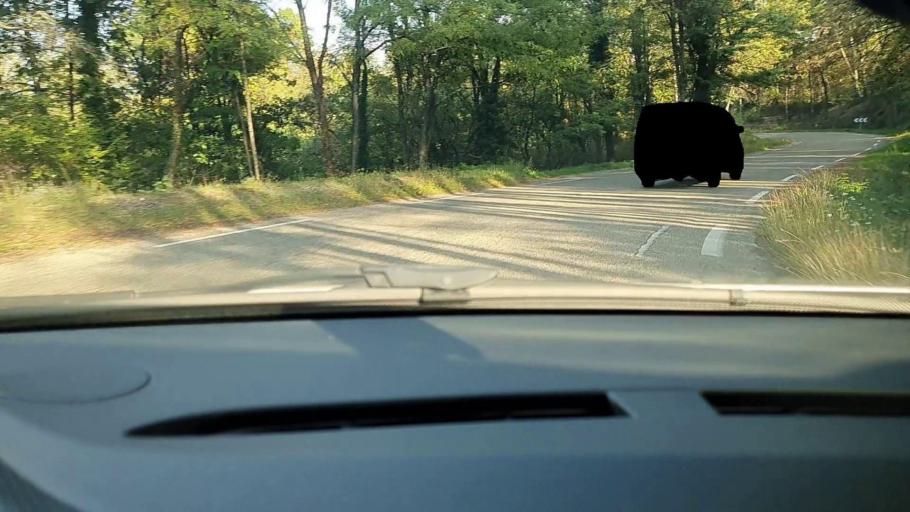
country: FR
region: Languedoc-Roussillon
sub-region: Departement du Gard
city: Besseges
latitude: 44.3161
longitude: 4.1360
